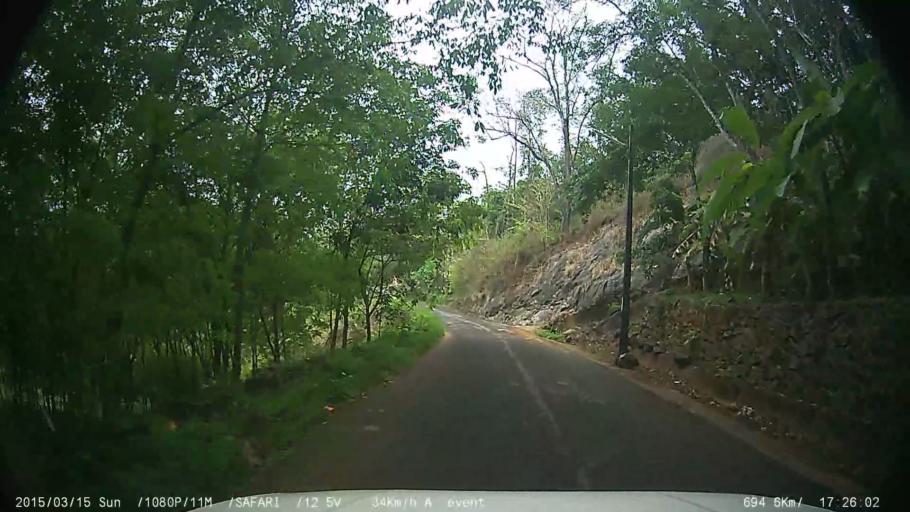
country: IN
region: Kerala
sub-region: Kottayam
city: Lalam
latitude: 9.8222
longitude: 76.7211
